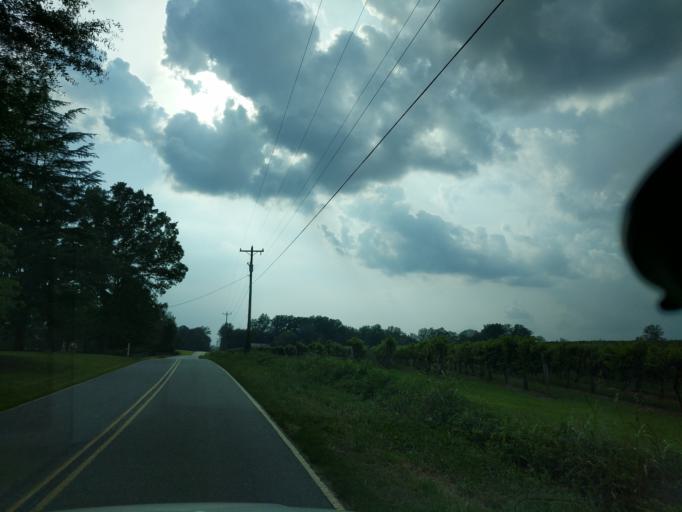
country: US
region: North Carolina
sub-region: Rutherford County
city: Rutherfordton
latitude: 35.2122
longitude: -82.0153
